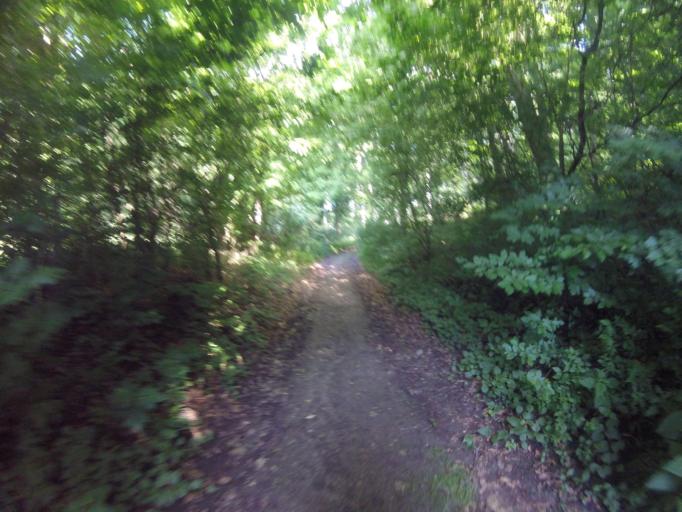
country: HU
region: Fejer
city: Bakonycsernye
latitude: 47.2665
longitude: 18.0441
